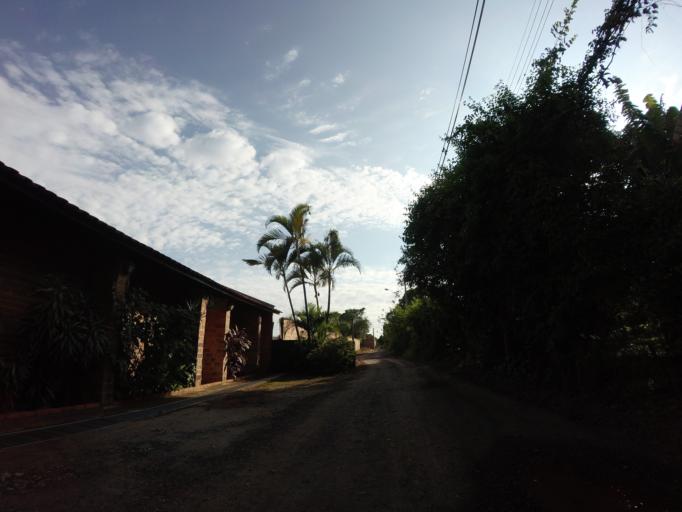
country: BR
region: Sao Paulo
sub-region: Piracicaba
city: Piracicaba
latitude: -22.7348
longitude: -47.5993
